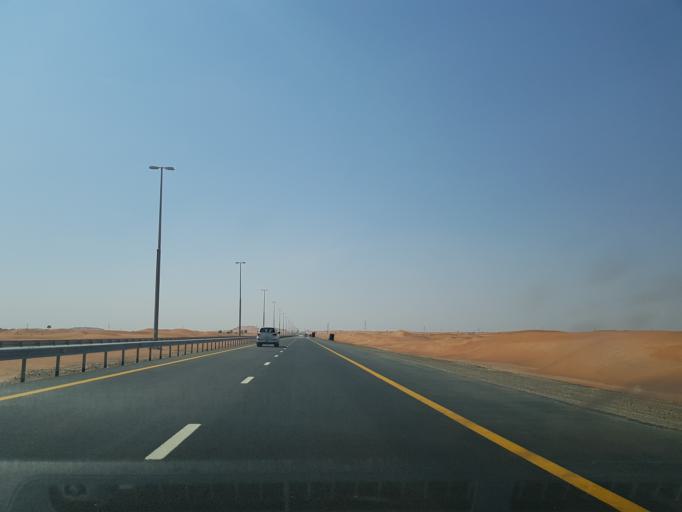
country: AE
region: Ash Shariqah
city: Adh Dhayd
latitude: 25.2410
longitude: 55.8796
